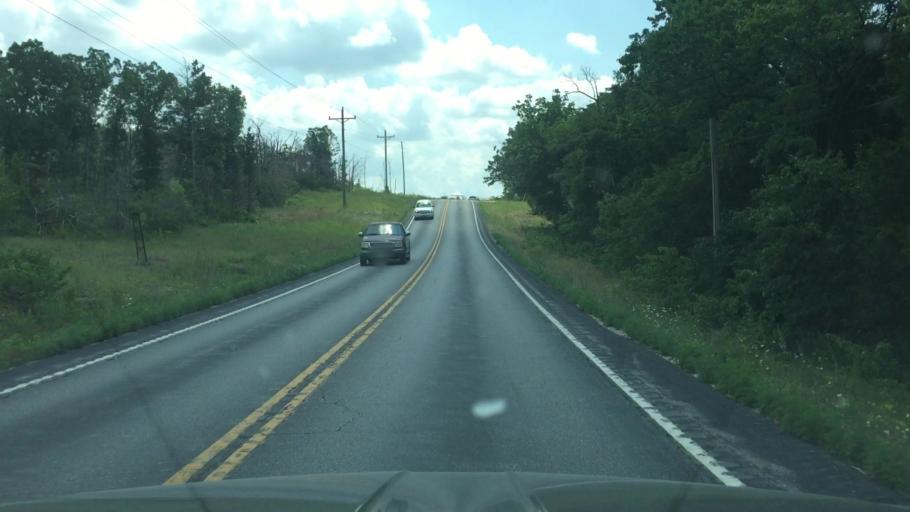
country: US
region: Missouri
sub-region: Miller County
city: Tuscumbia
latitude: 38.1120
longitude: -92.5048
